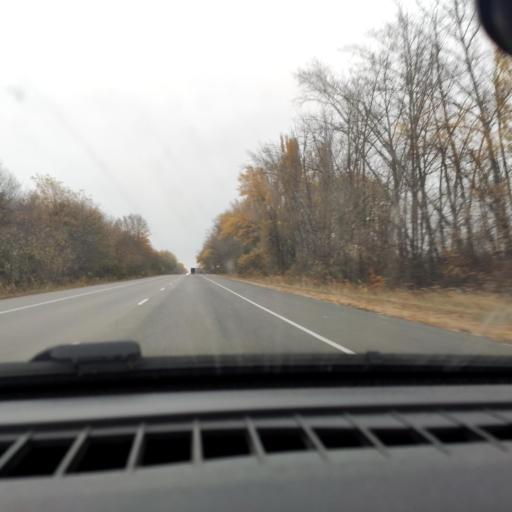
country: RU
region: Voronezj
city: Uryv-Pokrovka
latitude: 51.1643
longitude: 39.0707
